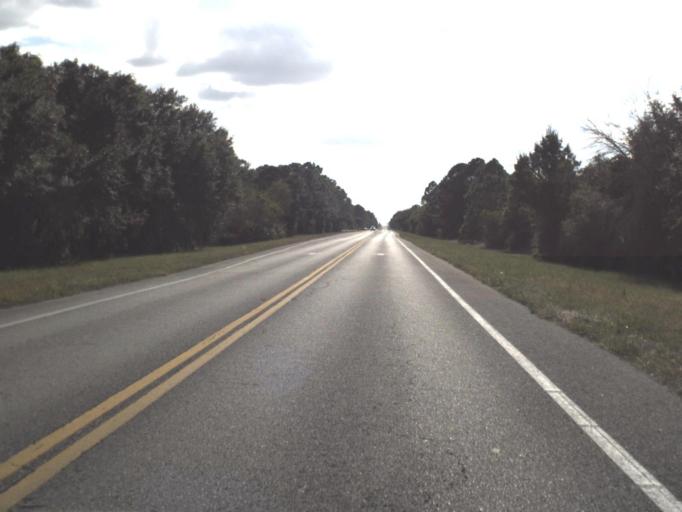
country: US
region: Florida
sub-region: Brevard County
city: Port Saint John
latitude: 28.5211
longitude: -80.8254
